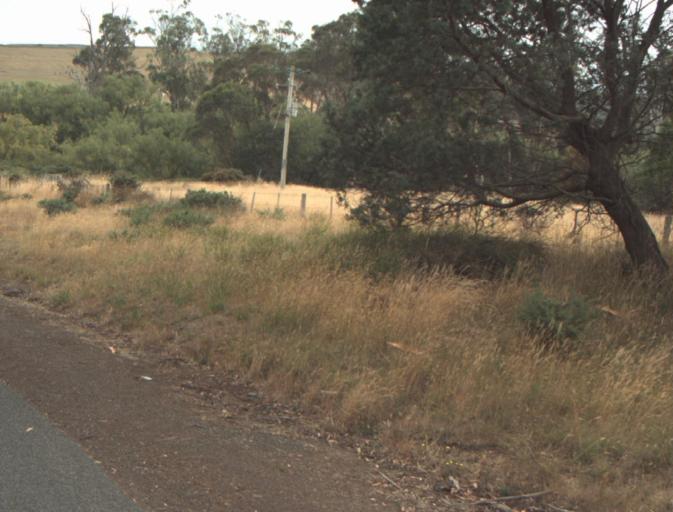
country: AU
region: Tasmania
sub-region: Northern Midlands
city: Evandale
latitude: -41.4818
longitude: 147.5040
